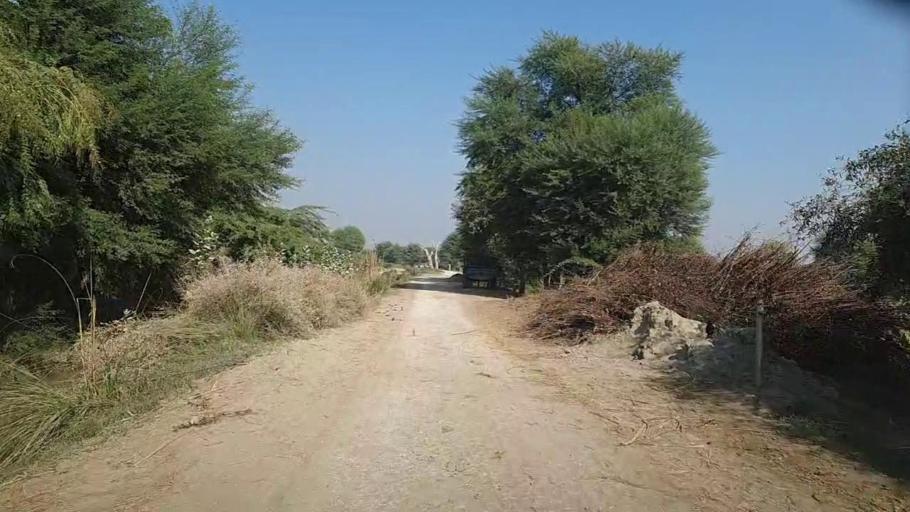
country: PK
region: Sindh
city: Bozdar
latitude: 27.1954
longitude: 68.6371
